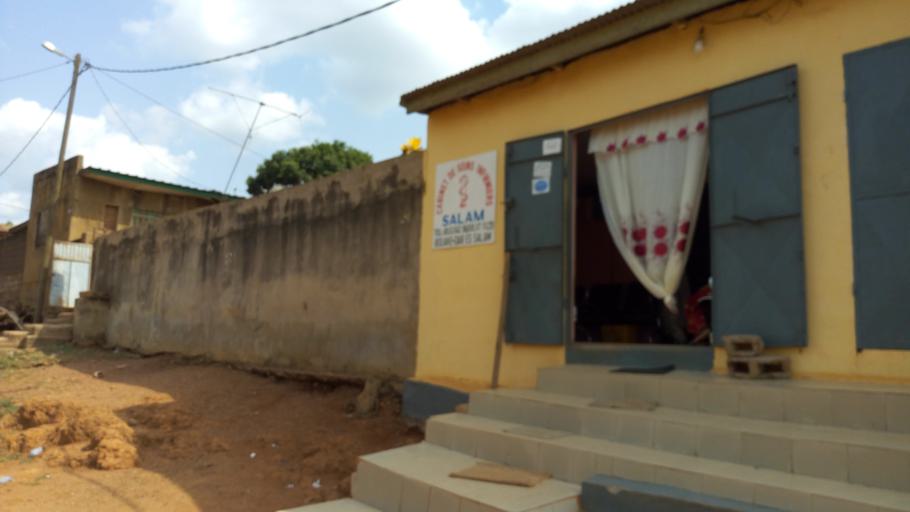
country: CI
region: Vallee du Bandama
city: Bouake
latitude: 7.7223
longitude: -5.0356
